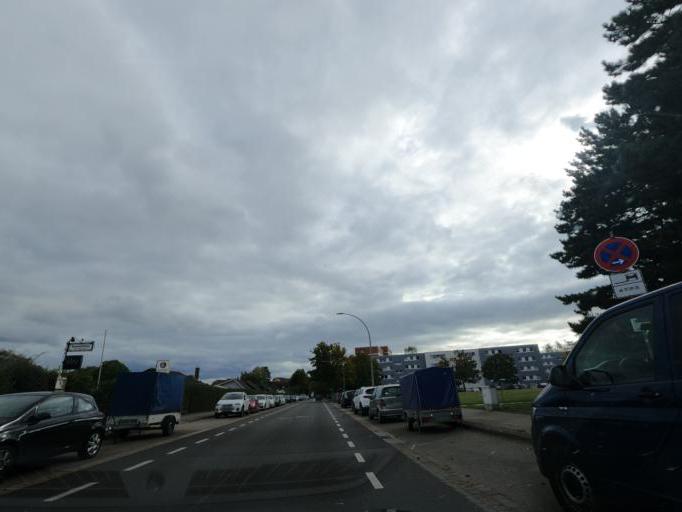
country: DE
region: Lower Saxony
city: Braunschweig
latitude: 52.2475
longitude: 10.4809
